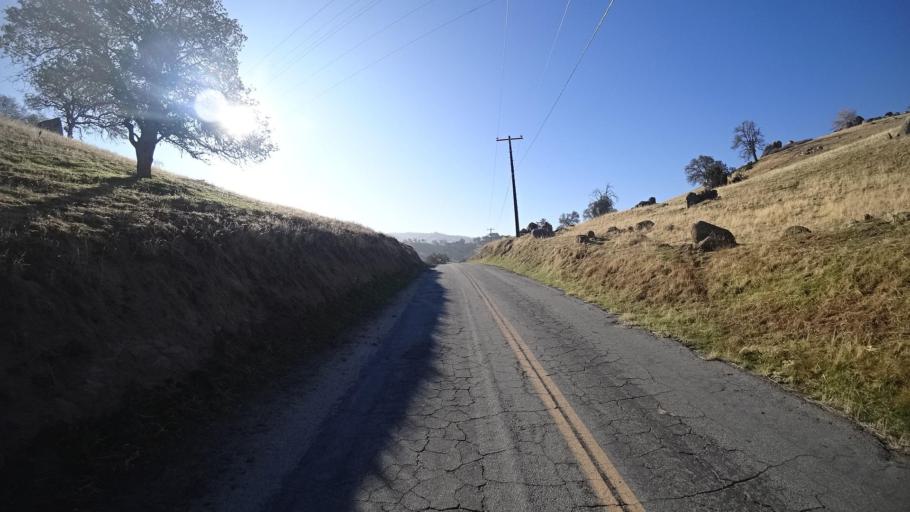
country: US
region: California
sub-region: Kern County
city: Alta Sierra
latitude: 35.7255
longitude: -118.8099
